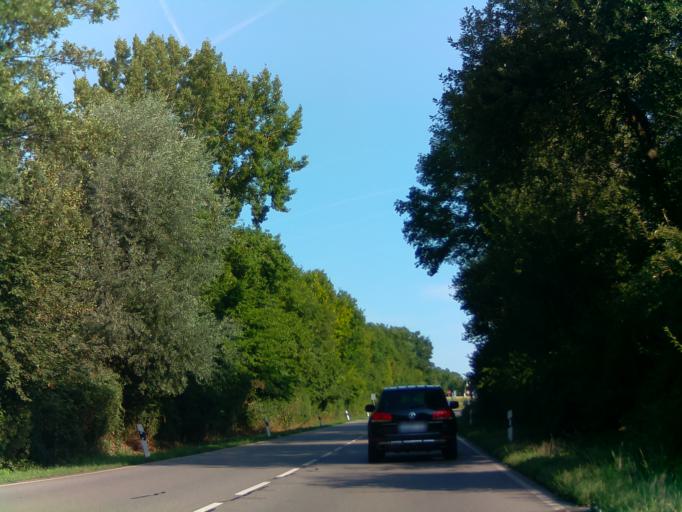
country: DE
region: Baden-Wuerttemberg
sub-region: Karlsruhe Region
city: Weinheim
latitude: 49.5541
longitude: 8.6499
